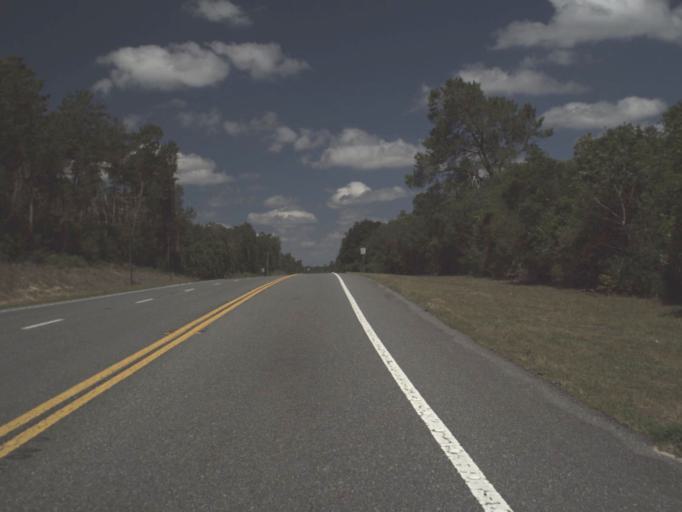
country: US
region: Florida
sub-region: Lake County
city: Astor
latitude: 29.1742
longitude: -81.6928
